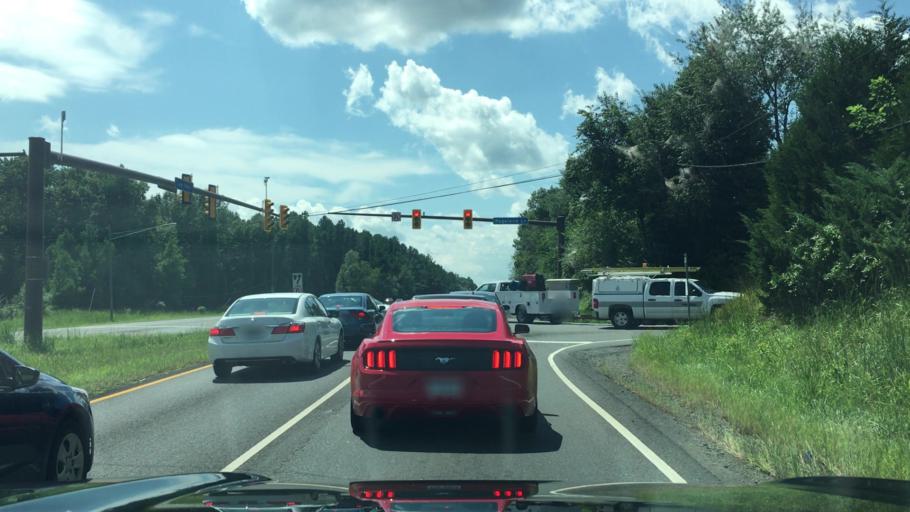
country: US
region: Virginia
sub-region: Prince William County
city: Gainesville
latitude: 38.8063
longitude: -77.5729
